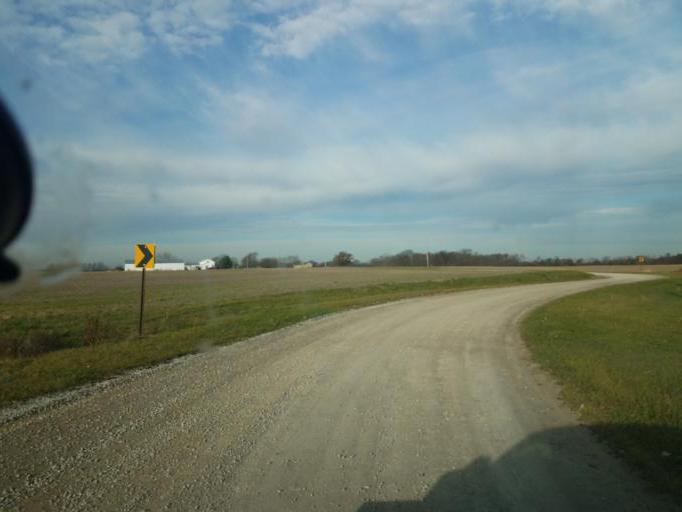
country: US
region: Ohio
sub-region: Morrow County
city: Mount Gilead
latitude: 40.5783
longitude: -82.8715
